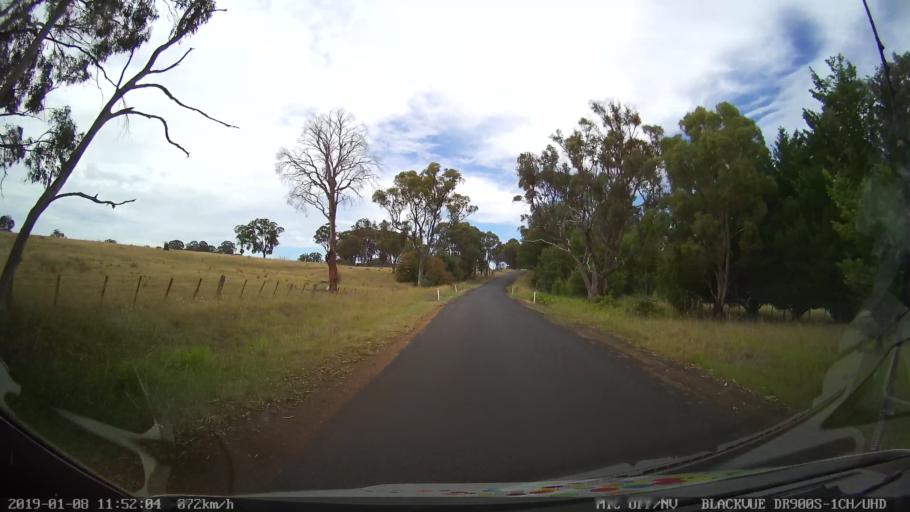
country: AU
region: New South Wales
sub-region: Armidale Dumaresq
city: Armidale
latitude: -30.3999
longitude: 151.5610
